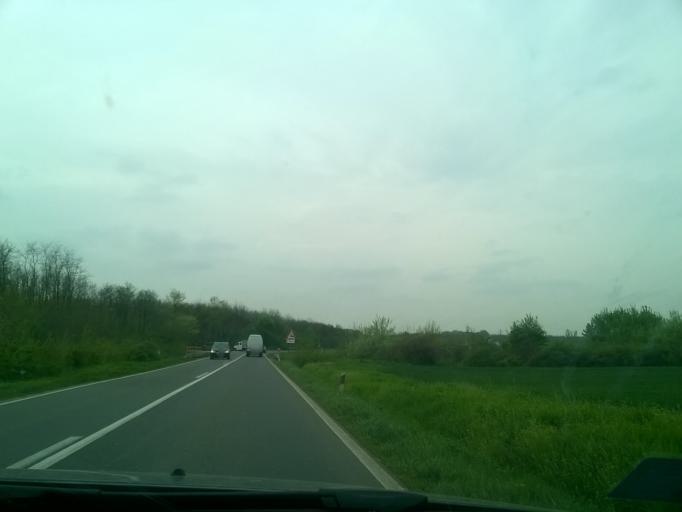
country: RS
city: Platicevo
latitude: 44.8109
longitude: 19.7605
